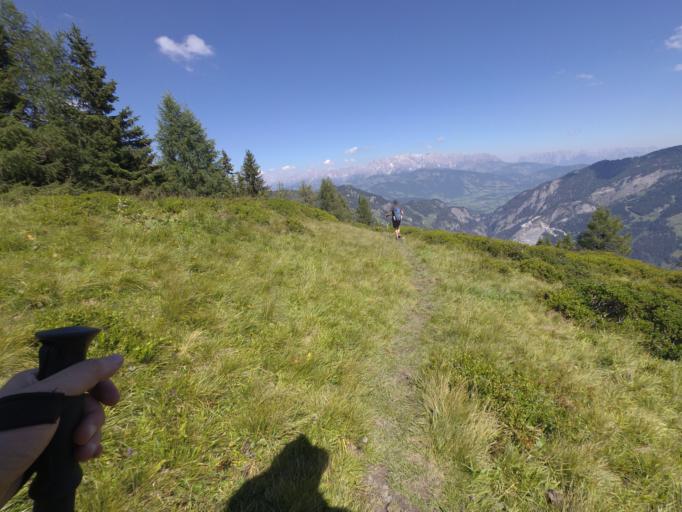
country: AT
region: Salzburg
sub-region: Politischer Bezirk Sankt Johann im Pongau
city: Dorfgastein
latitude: 47.2396
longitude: 13.0628
